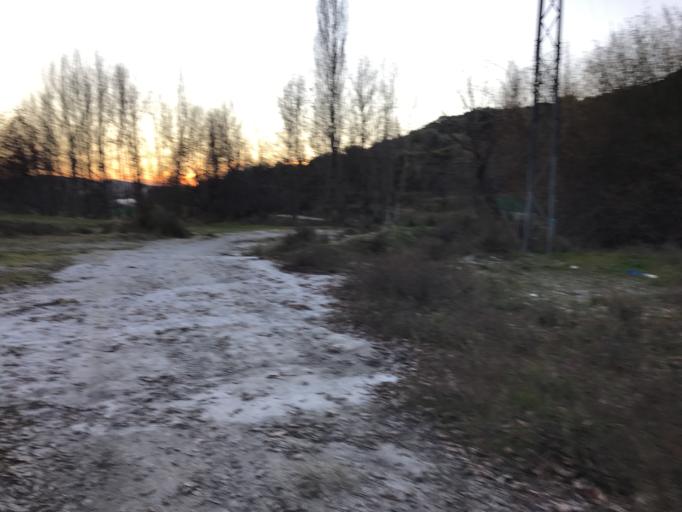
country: ES
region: Andalusia
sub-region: Provincia de Granada
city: Beas de Granada
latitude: 37.2287
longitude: -3.4745
